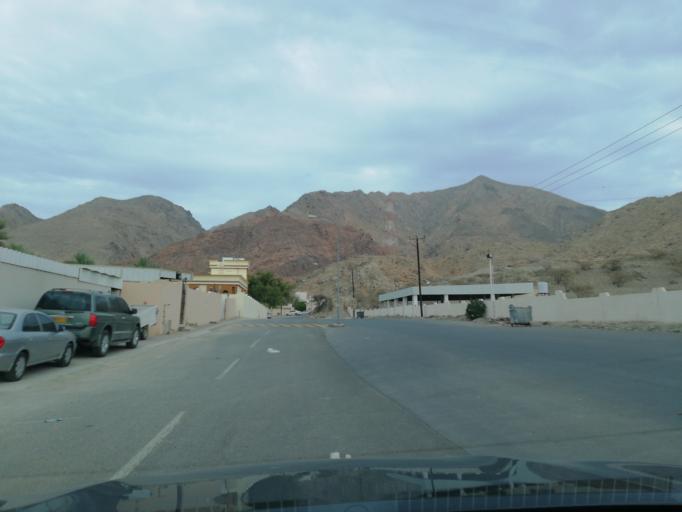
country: OM
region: Muhafazat Masqat
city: Bawshar
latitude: 23.4862
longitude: 58.3455
